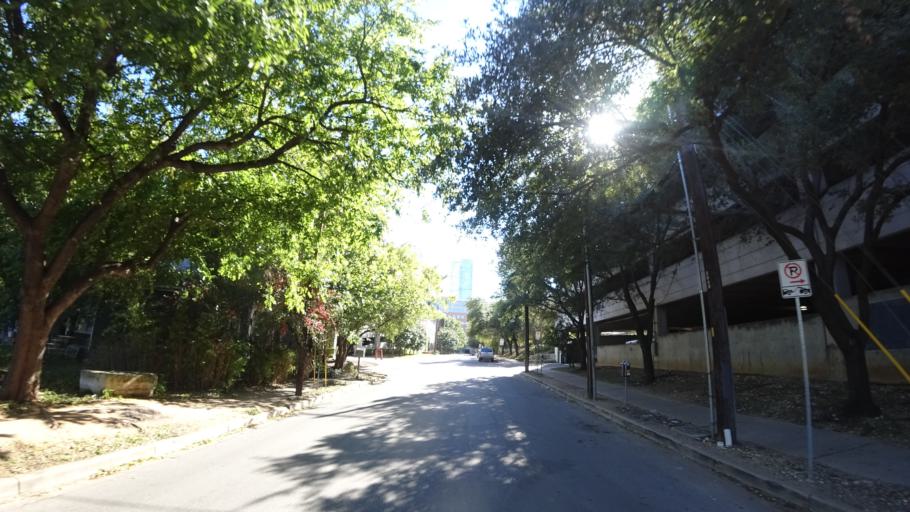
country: US
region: Texas
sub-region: Travis County
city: Austin
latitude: 30.2730
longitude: -97.7520
